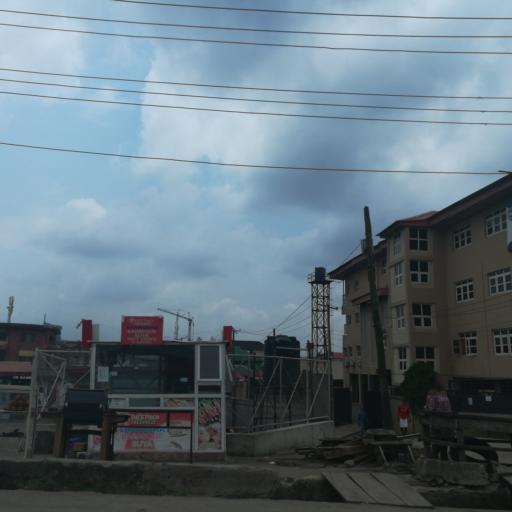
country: NG
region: Lagos
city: Ojota
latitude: 6.5855
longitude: 3.3842
